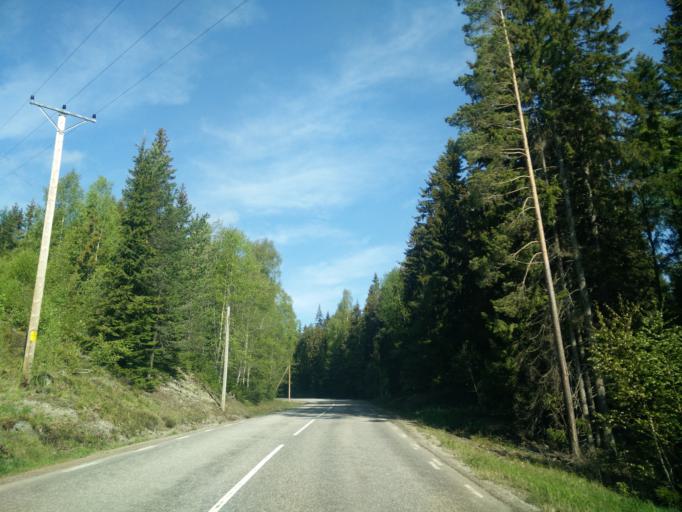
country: SE
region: Vaesternorrland
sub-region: Sundsvalls Kommun
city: Nolby
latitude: 62.3002
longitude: 17.3176
